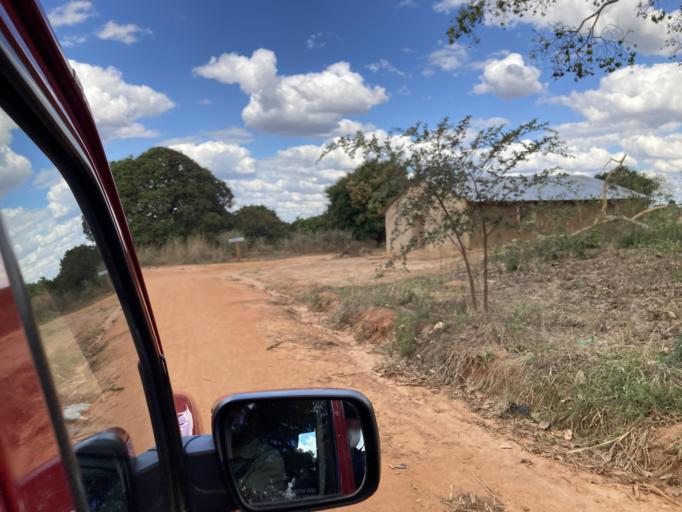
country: MZ
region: Cabo Delgado
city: Montepuez
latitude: -13.1266
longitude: 39.0330
